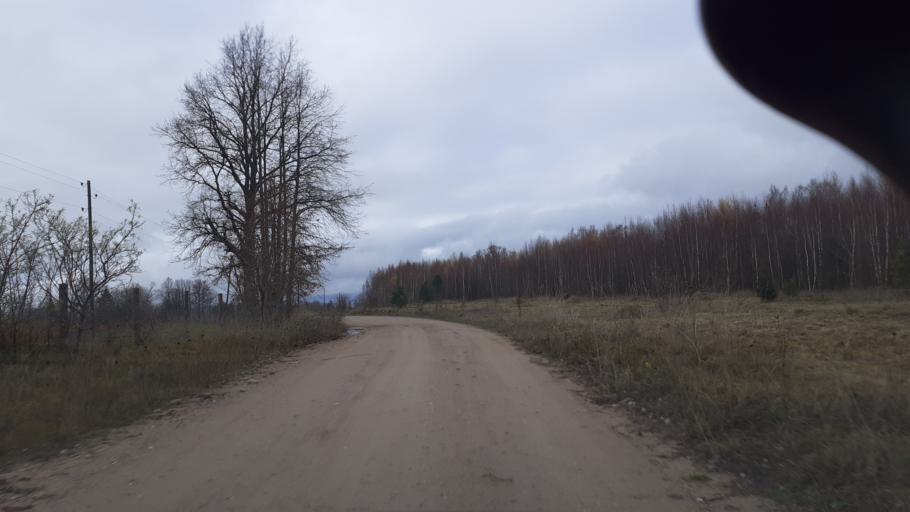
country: LV
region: Kuldigas Rajons
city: Kuldiga
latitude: 57.0416
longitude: 21.8767
